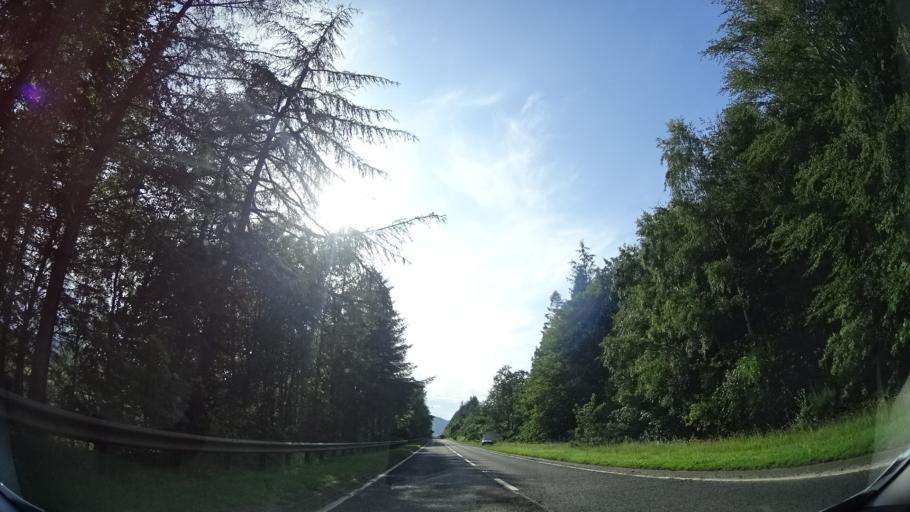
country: GB
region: Scotland
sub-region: Highland
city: Muir of Ord
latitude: 57.5583
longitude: -4.5145
